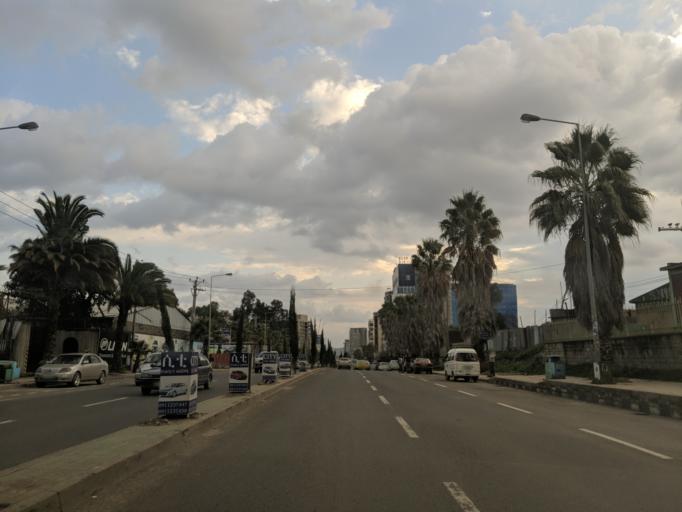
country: ET
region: Adis Abeba
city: Addis Ababa
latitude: 8.9874
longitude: 38.7701
